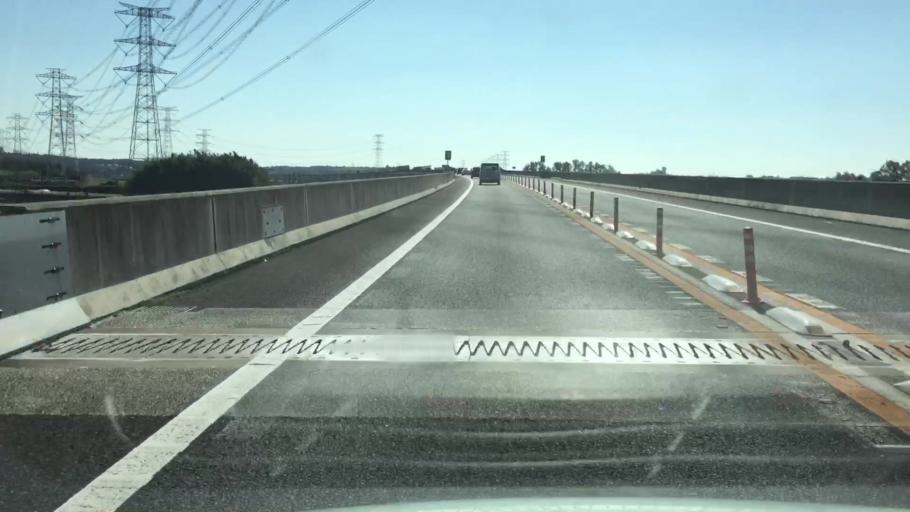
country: JP
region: Ibaraki
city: Ushiku
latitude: 35.9999
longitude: 140.1489
